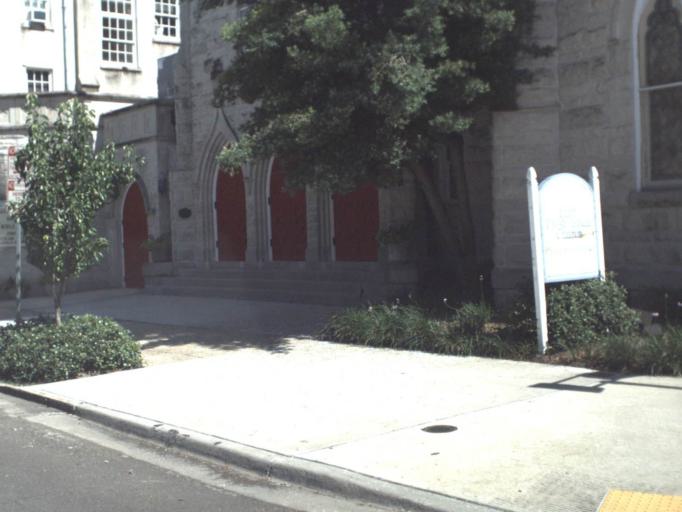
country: US
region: Florida
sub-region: Duval County
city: Jacksonville
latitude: 30.3282
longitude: -81.6560
